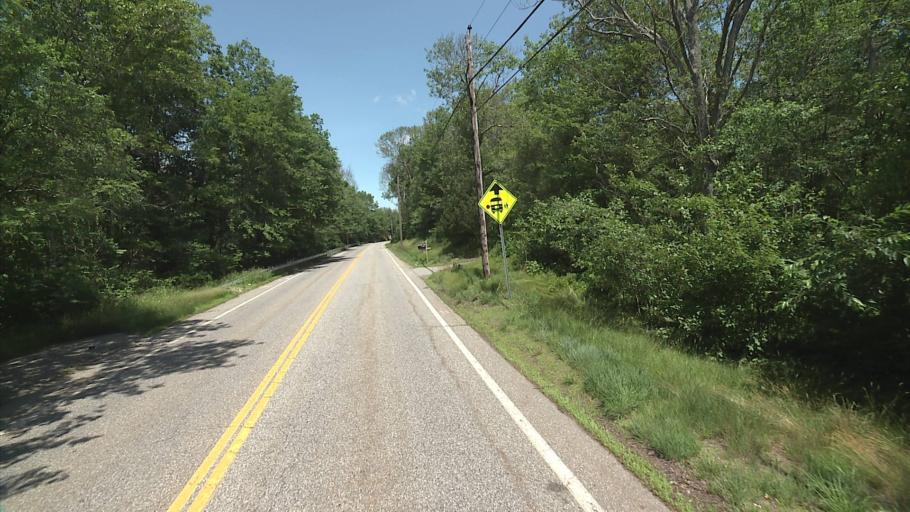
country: US
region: Connecticut
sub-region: New London County
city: Preston City
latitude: 41.4892
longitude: -71.9008
